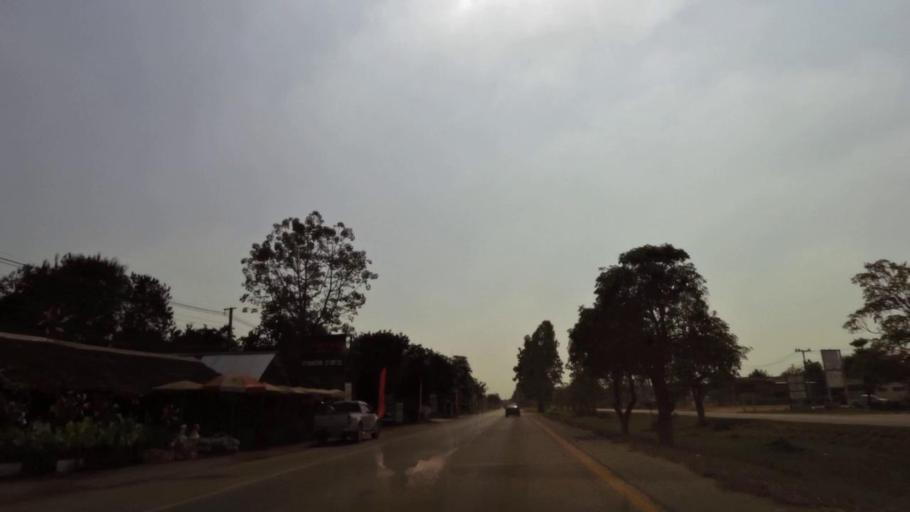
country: TH
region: Phichit
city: Wachira Barami
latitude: 16.5024
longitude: 100.1437
